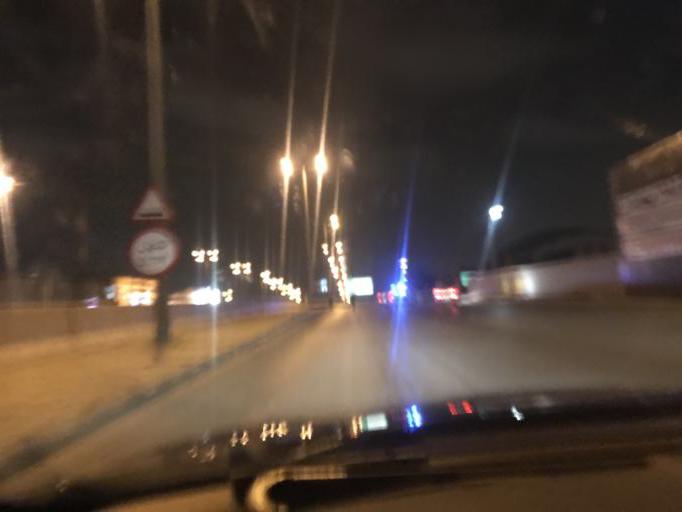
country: SA
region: Ar Riyad
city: Riyadh
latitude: 24.7813
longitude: 46.7060
